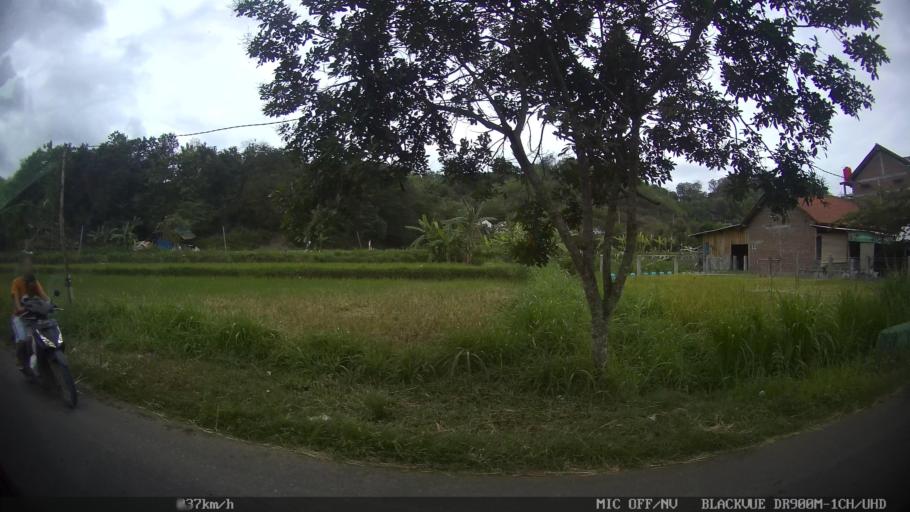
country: ID
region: Daerah Istimewa Yogyakarta
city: Sewon
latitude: -7.8643
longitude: 110.4210
